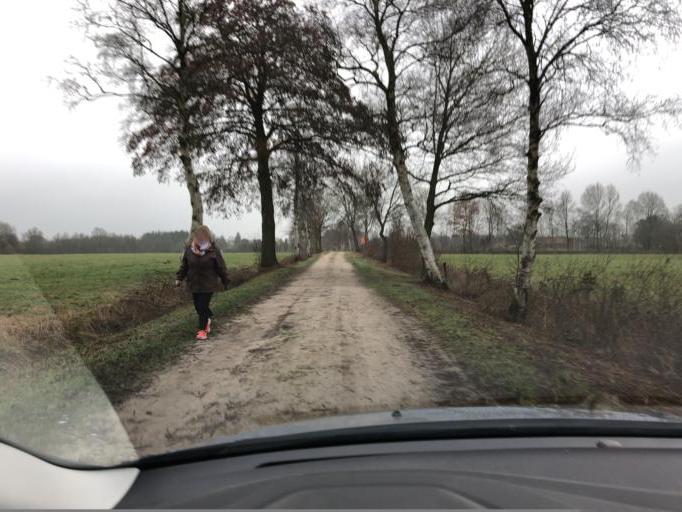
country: DE
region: Lower Saxony
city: Bad Zwischenahn
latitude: 53.1727
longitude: 8.0443
